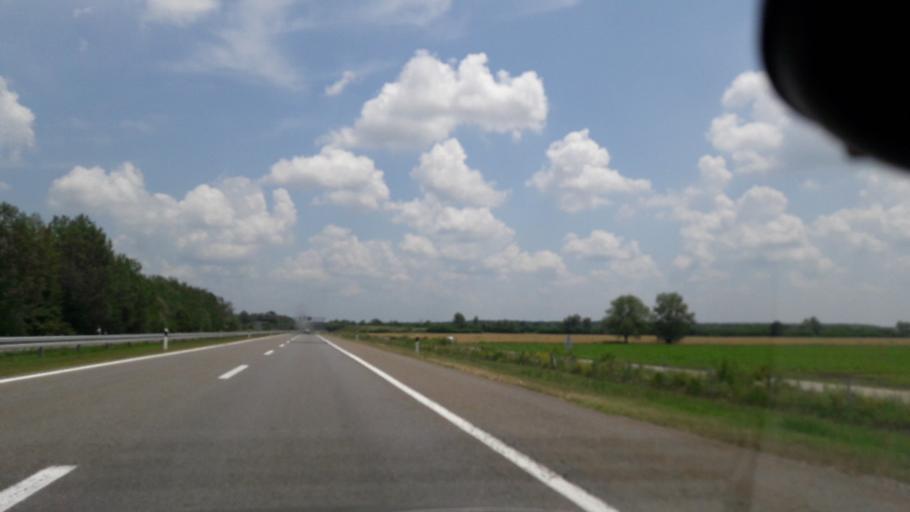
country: HR
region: Vukovarsko-Srijemska
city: Zupanja
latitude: 45.0992
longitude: 18.7253
